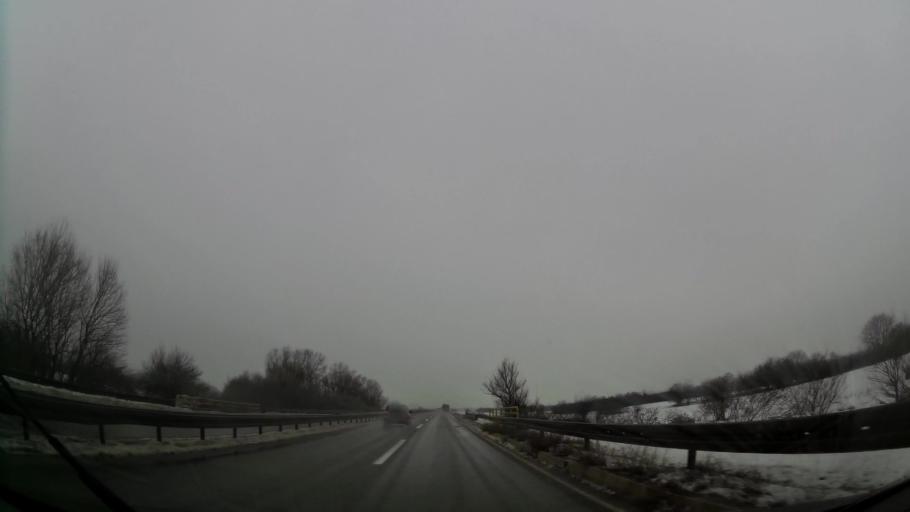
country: RS
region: Central Serbia
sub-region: Belgrade
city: Cukarica
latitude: 44.7518
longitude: 20.3781
